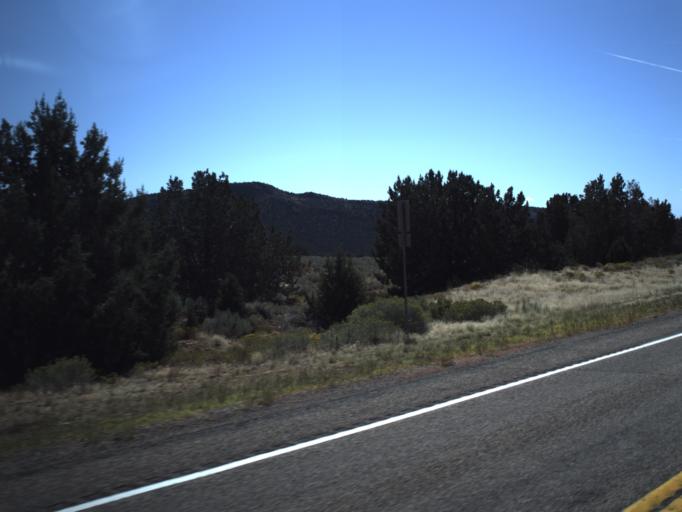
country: US
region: Utah
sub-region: Washington County
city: Enterprise
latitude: 37.3930
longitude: -113.6461
